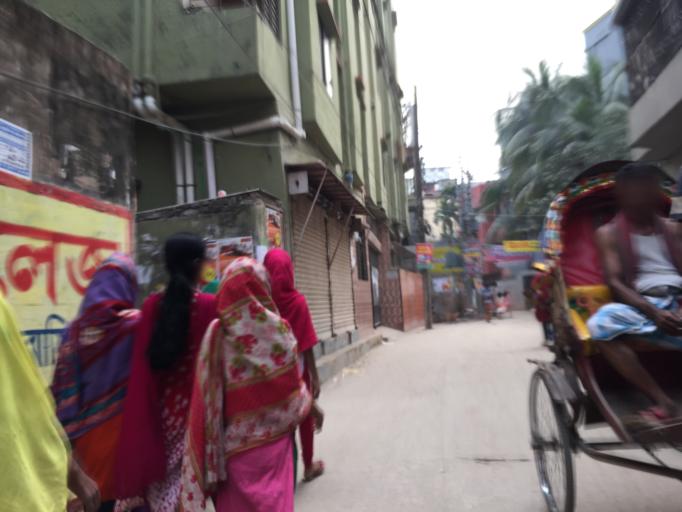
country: BD
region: Dhaka
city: Azimpur
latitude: 23.7951
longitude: 90.3617
